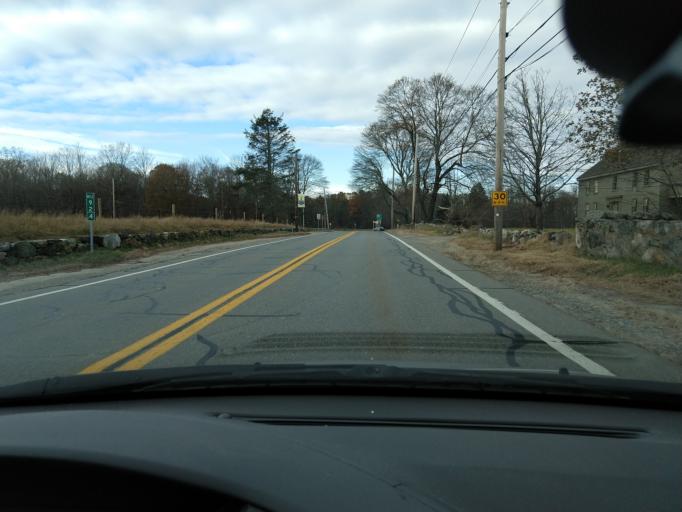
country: US
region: Massachusetts
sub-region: Middlesex County
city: Lincoln
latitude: 42.4531
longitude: -71.3083
